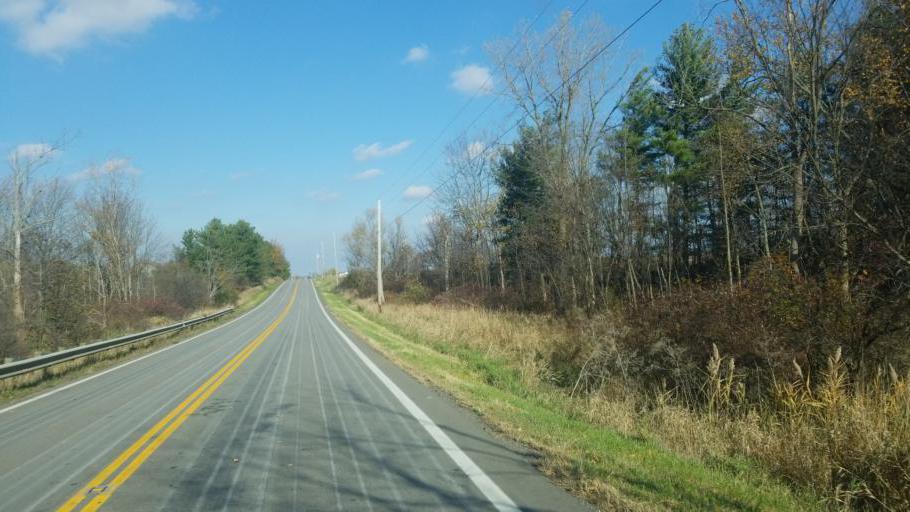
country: US
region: Ohio
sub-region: Huron County
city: New London
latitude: 41.0623
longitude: -82.3042
